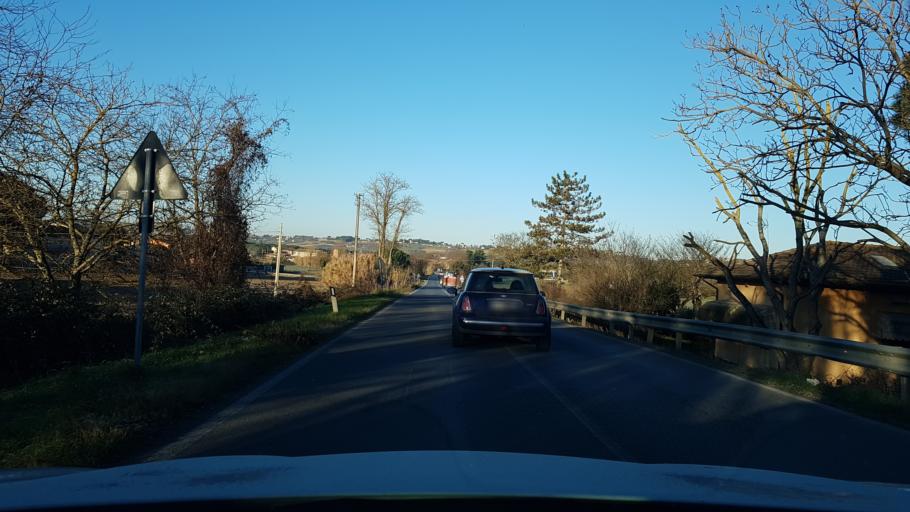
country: IT
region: Umbria
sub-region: Provincia di Perugia
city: San Martino in Campo
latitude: 43.0356
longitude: 12.4210
